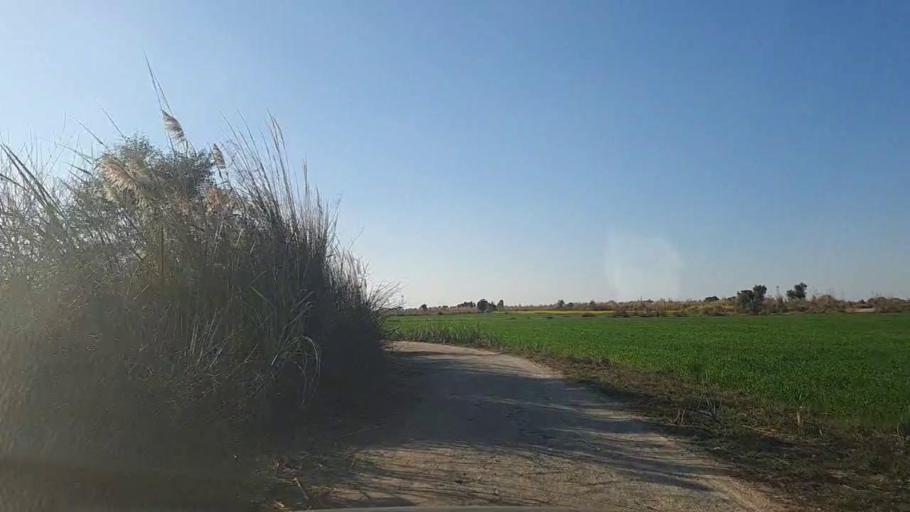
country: PK
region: Sindh
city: Khadro
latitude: 26.2413
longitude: 68.8653
